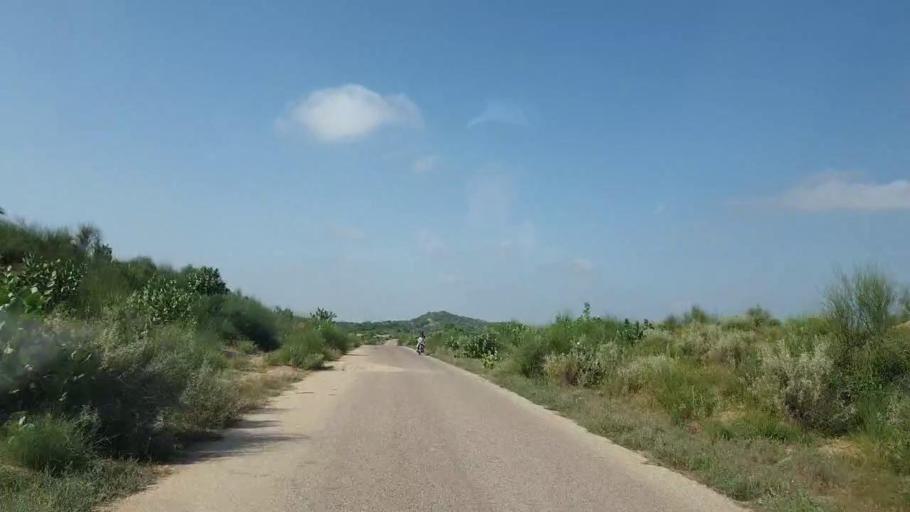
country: PK
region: Sindh
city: Mithi
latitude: 24.5553
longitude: 69.8936
